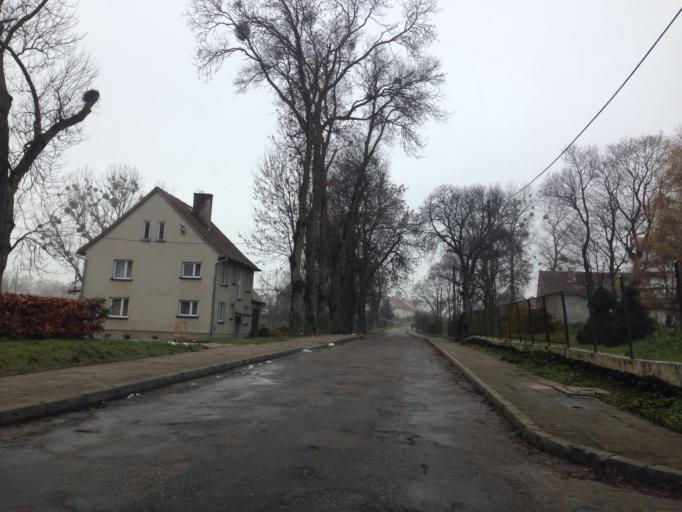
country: PL
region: Warmian-Masurian Voivodeship
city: Gierloz
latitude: 54.0075
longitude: 21.4523
